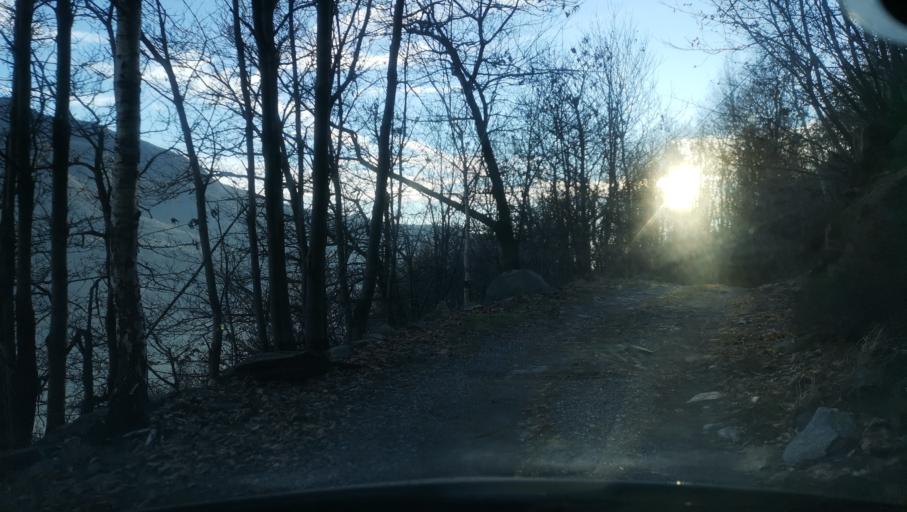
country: IT
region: Piedmont
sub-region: Provincia di Torino
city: Tavagnasco
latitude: 45.5385
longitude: 7.8190
